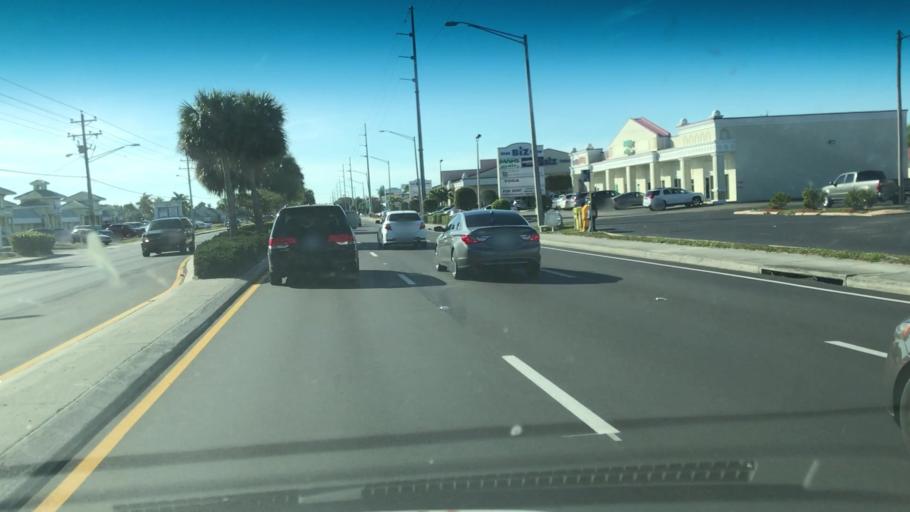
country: US
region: Florida
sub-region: Lee County
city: Cape Coral
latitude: 26.5957
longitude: -81.9417
